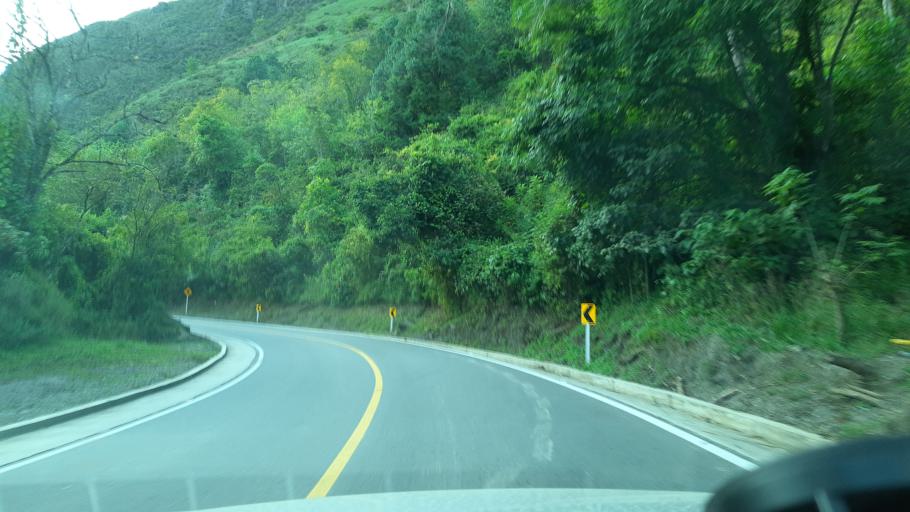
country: CO
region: Boyaca
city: Somondoco
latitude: 4.9856
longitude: -73.3460
